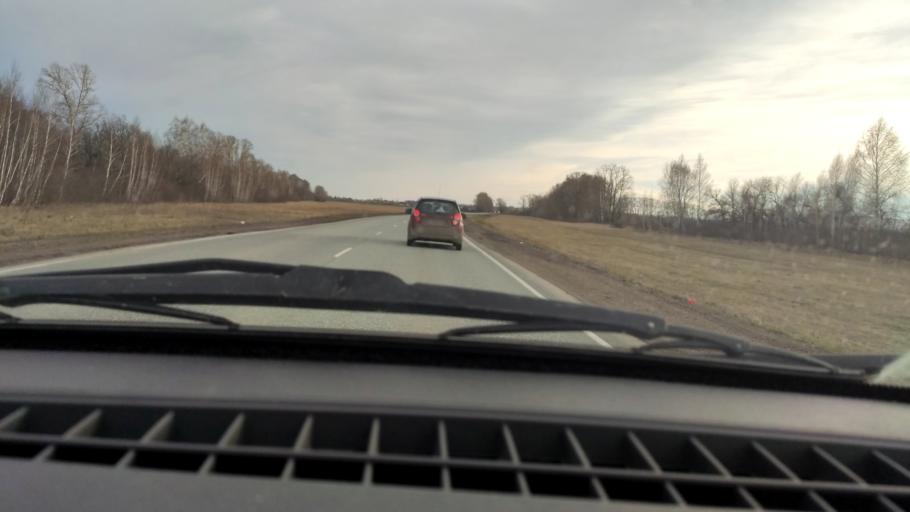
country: RU
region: Bashkortostan
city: Chishmy
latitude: 54.4109
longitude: 55.2220
